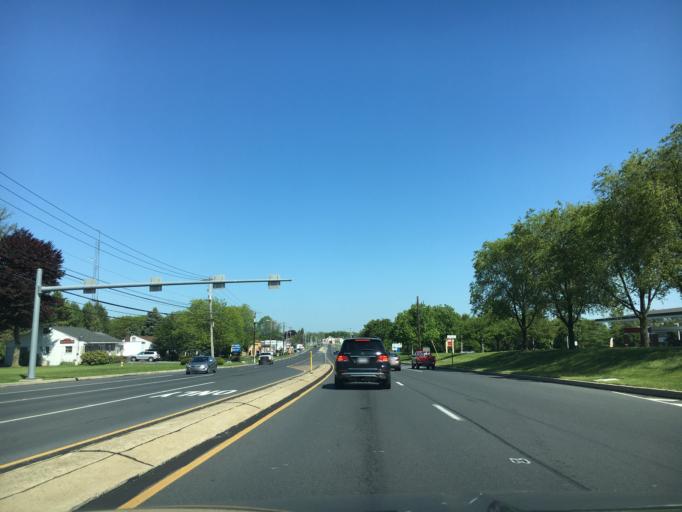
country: US
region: Pennsylvania
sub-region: Lehigh County
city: Catasauqua
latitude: 40.6579
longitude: -75.4184
